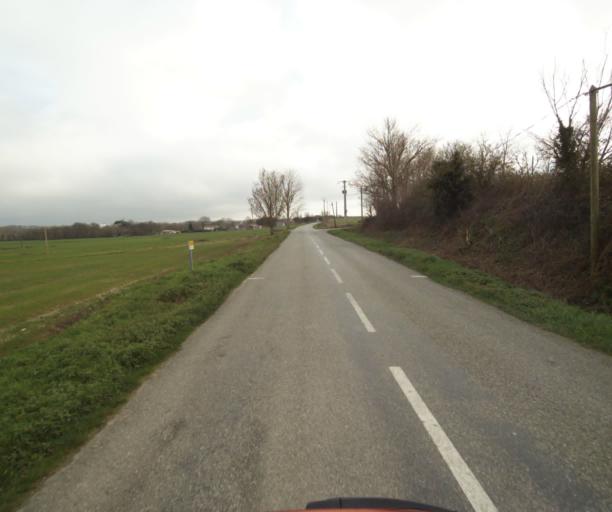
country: FR
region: Languedoc-Roussillon
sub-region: Departement de l'Aude
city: Belpech
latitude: 43.2061
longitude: 1.7311
